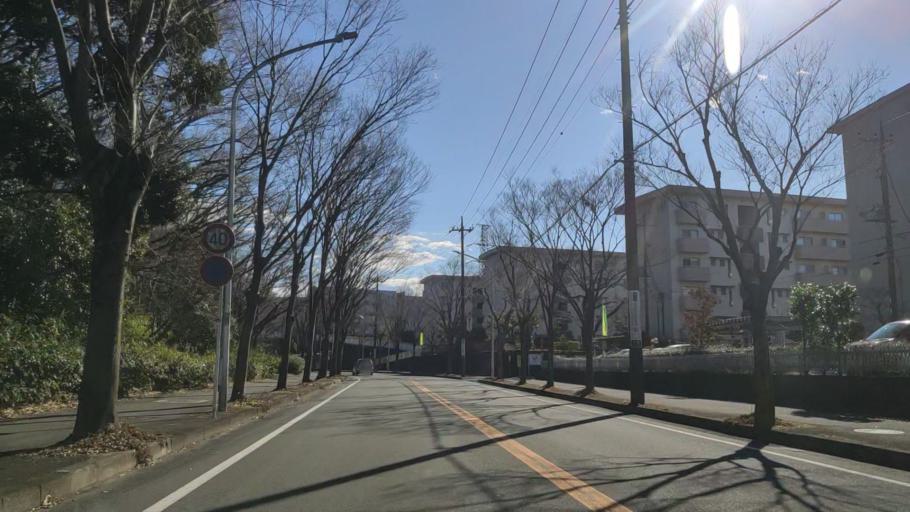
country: JP
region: Tokyo
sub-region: Machida-shi
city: Machida
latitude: 35.5137
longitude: 139.5006
